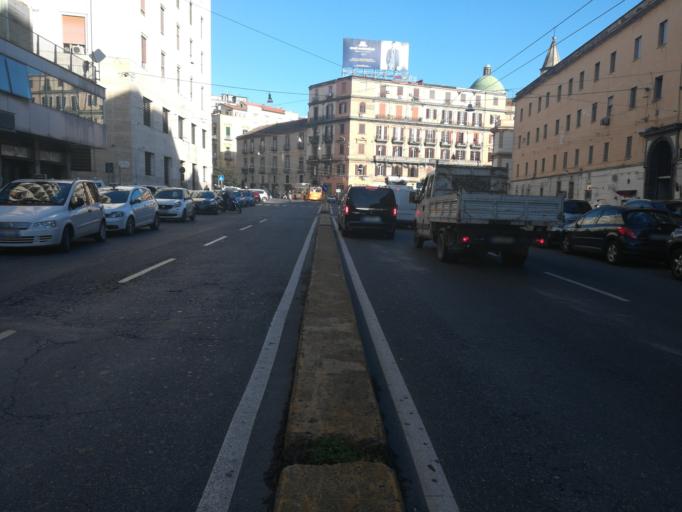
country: IT
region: Campania
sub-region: Provincia di Napoli
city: Napoli
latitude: 40.8421
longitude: 14.2525
